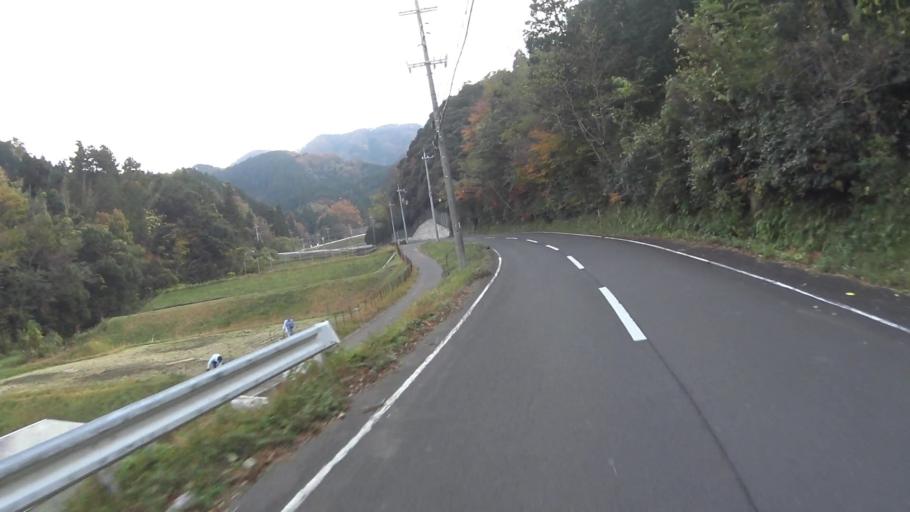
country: JP
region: Kyoto
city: Maizuru
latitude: 35.5621
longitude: 135.4540
